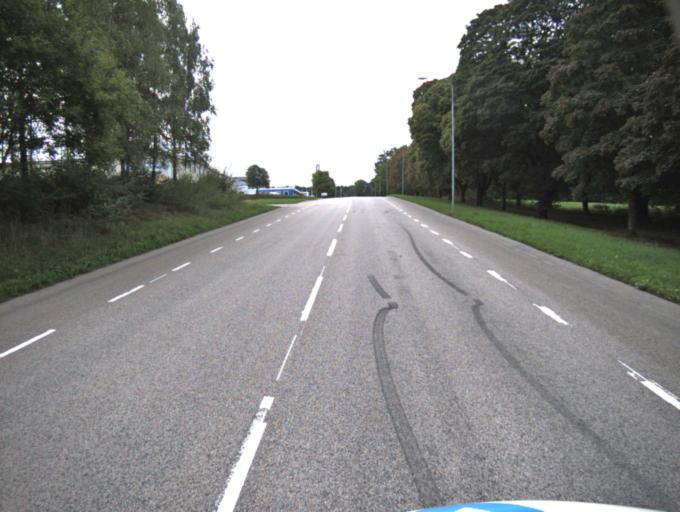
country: SE
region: Vaestra Goetaland
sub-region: Ulricehamns Kommun
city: Ulricehamn
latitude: 57.8026
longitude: 13.4404
